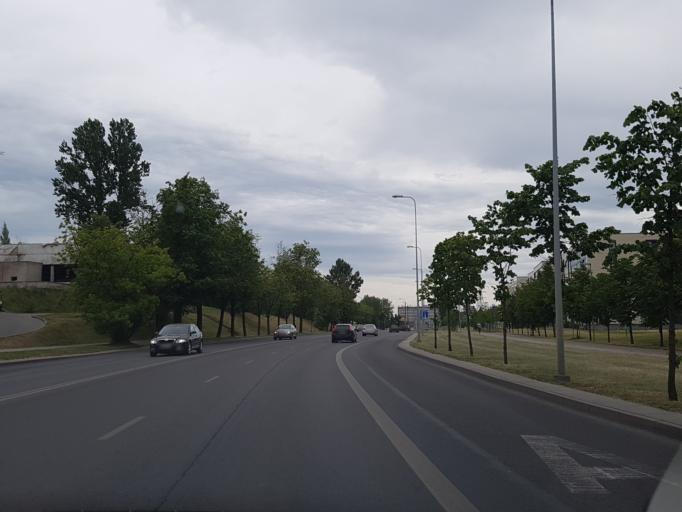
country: LT
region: Vilnius County
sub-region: Vilnius
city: Vilnius
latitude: 54.7201
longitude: 25.2864
